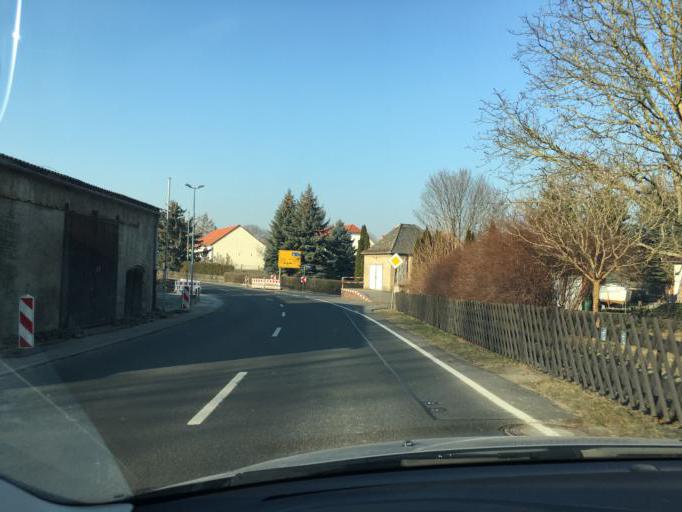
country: DE
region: Saxony
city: Kitzscher
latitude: 51.1218
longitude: 12.5899
